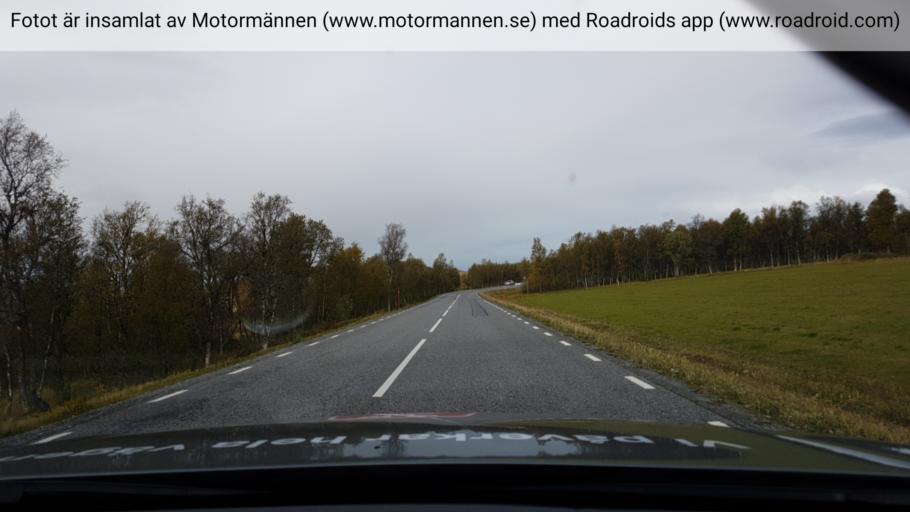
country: NO
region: Nord-Trondelag
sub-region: Meraker
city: Meraker
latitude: 63.5821
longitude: 12.2746
